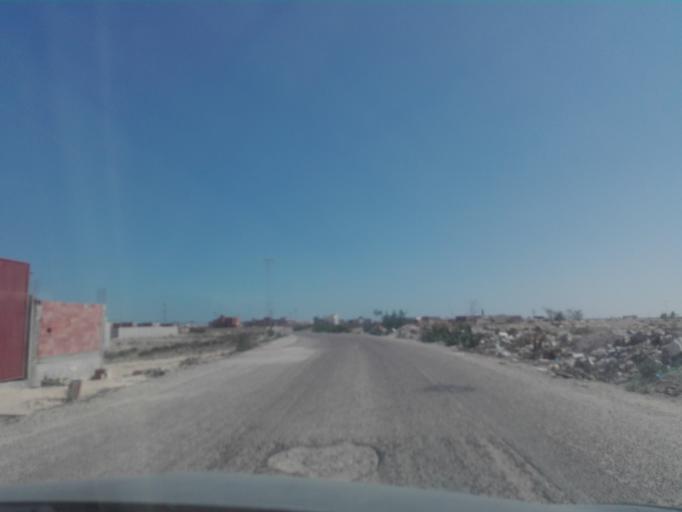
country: TN
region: Qabis
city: Gabes
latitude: 33.8707
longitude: 10.0426
